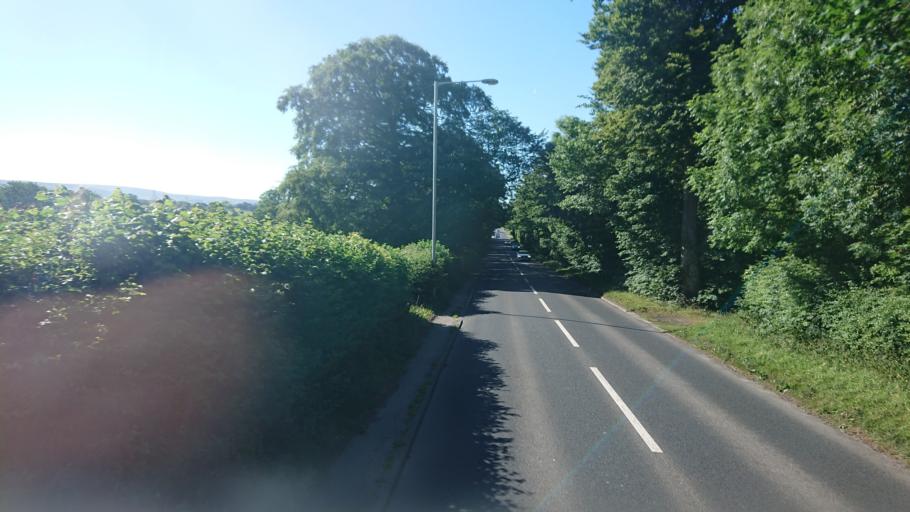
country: GB
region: England
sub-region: Lancashire
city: Bay Horse
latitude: 53.9701
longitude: -2.7817
